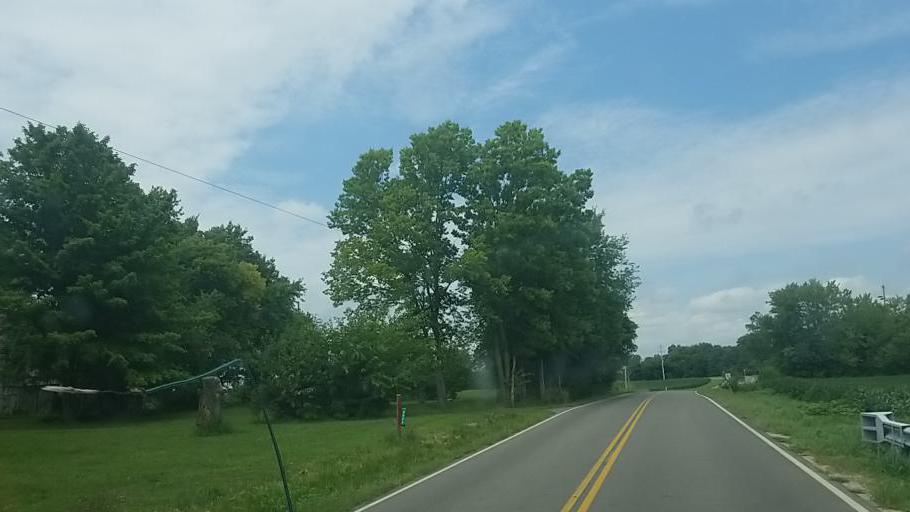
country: US
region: Ohio
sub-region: Pickaway County
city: Ashville
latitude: 39.7908
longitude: -82.9059
